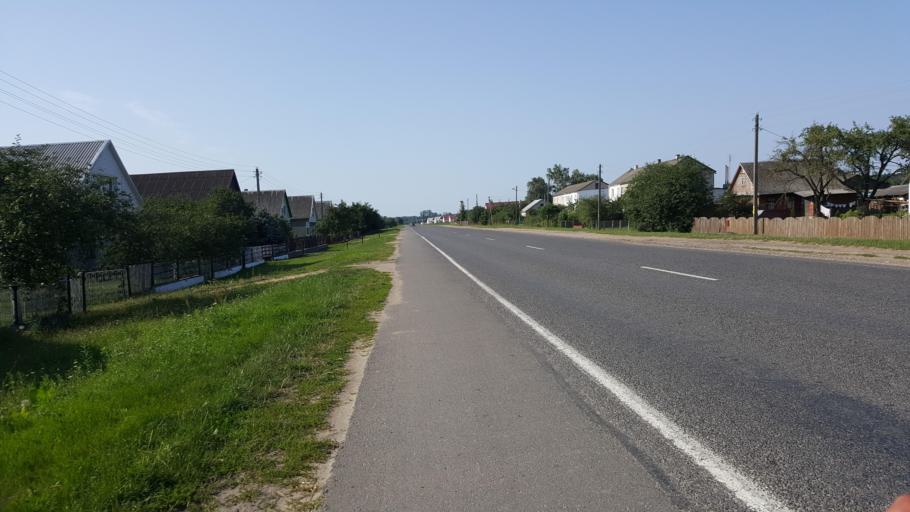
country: BY
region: Brest
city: Kamyanyets
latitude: 52.3214
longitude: 23.9184
